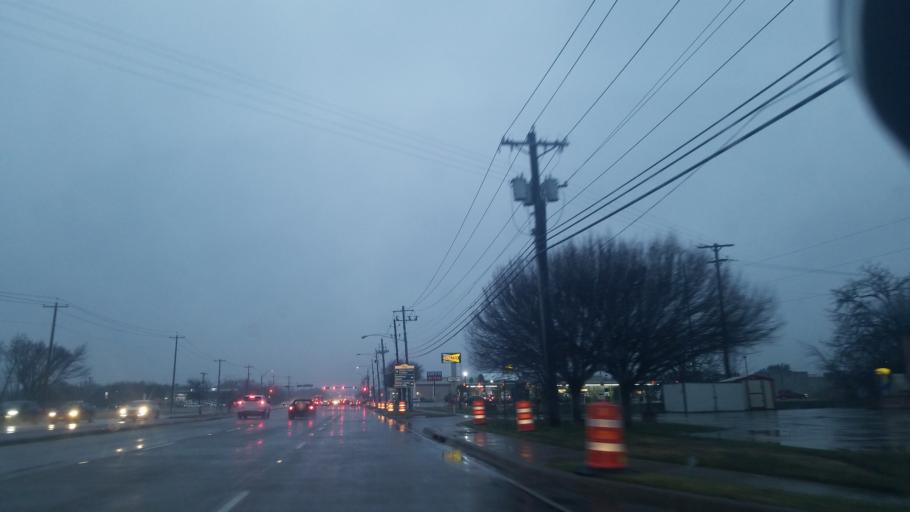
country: US
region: Texas
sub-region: Denton County
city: Denton
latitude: 33.2153
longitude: -97.0907
